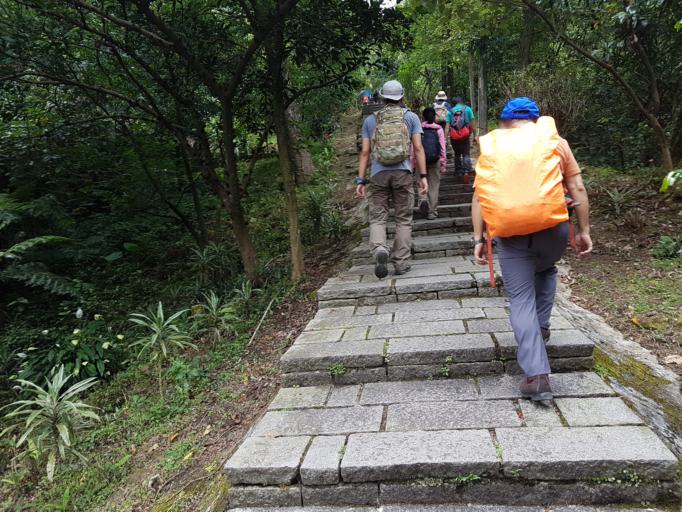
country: TW
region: Taiwan
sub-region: Keelung
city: Keelung
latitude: 25.0562
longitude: 121.6632
